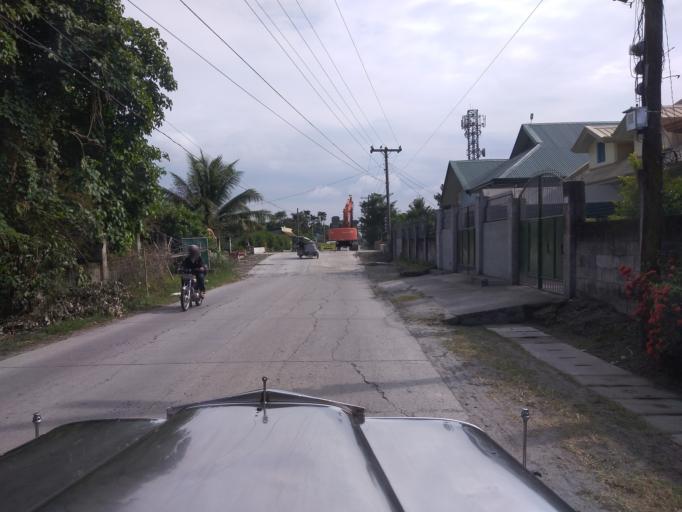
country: PH
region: Central Luzon
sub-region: Province of Pampanga
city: San Patricio
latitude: 15.0959
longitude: 120.7109
